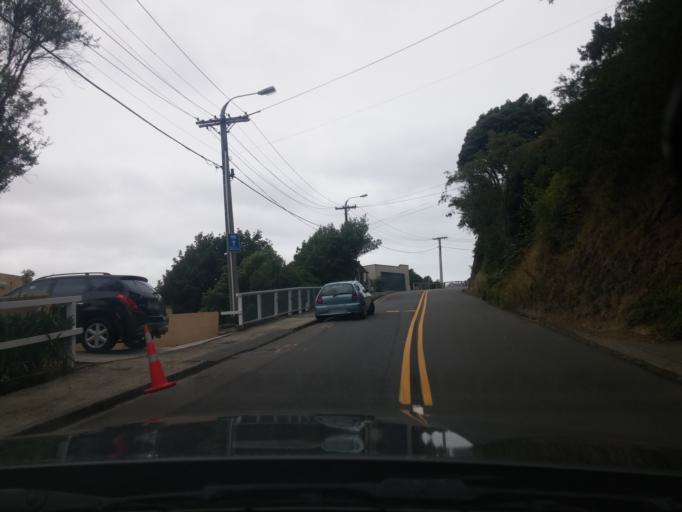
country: NZ
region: Wellington
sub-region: Wellington City
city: Kelburn
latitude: -41.2615
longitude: 174.7713
